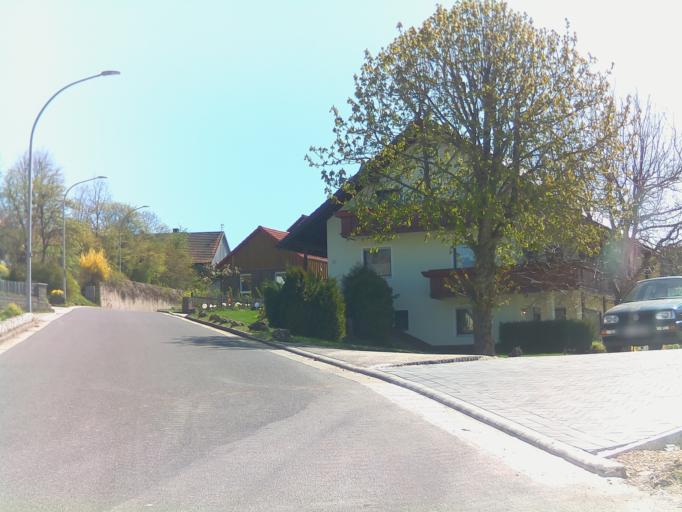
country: DE
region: Bavaria
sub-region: Upper Palatinate
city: Kastl
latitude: 49.4061
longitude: 11.6568
